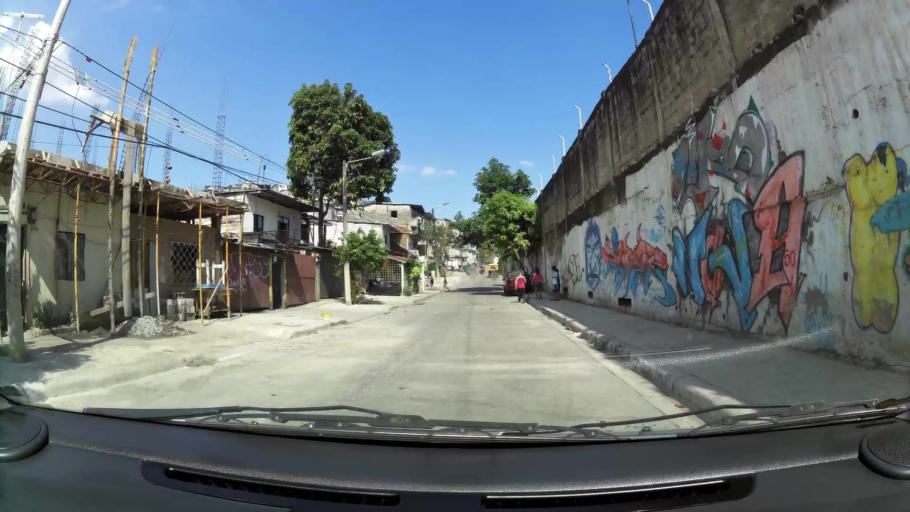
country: EC
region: Guayas
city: Guayaquil
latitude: -2.1514
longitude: -79.9406
